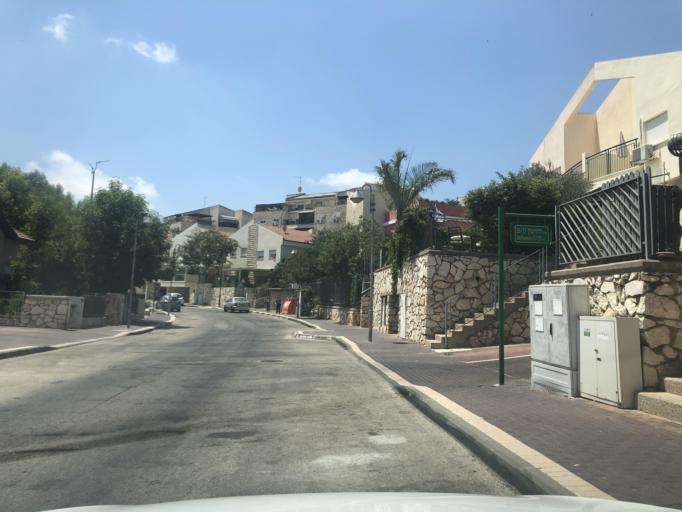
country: IL
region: Haifa
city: Daliyat el Karmil
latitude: 32.6363
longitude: 35.0901
